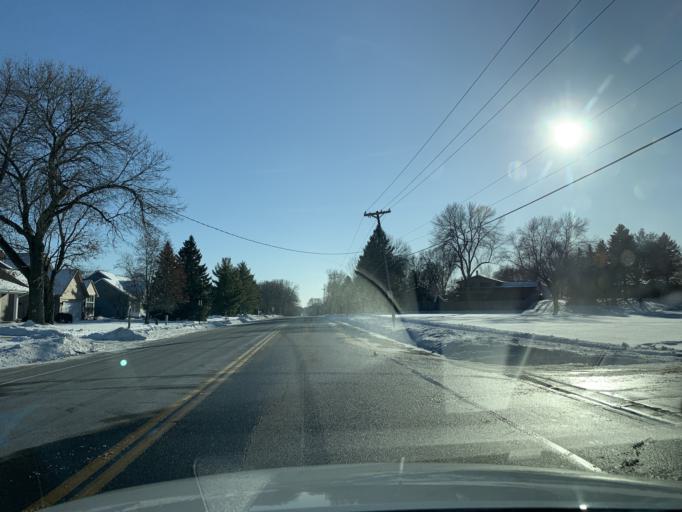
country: US
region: Minnesota
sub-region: Scott County
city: Savage
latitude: 44.8315
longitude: -93.3585
